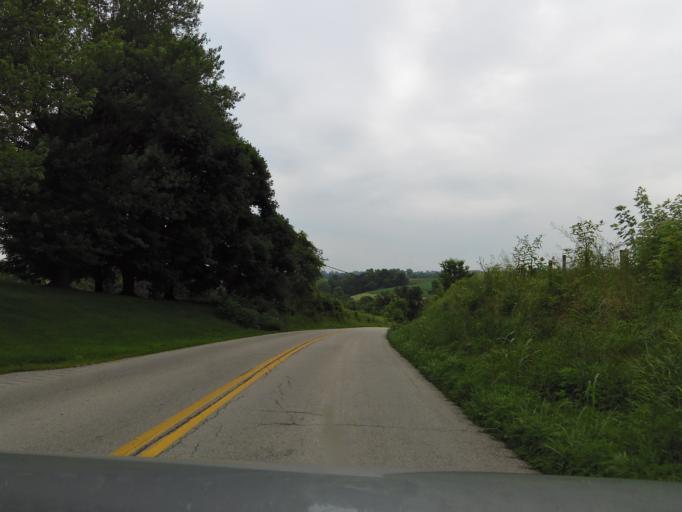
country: US
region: Kentucky
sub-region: Robertson County
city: Mount Olivet
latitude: 38.5201
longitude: -83.8989
